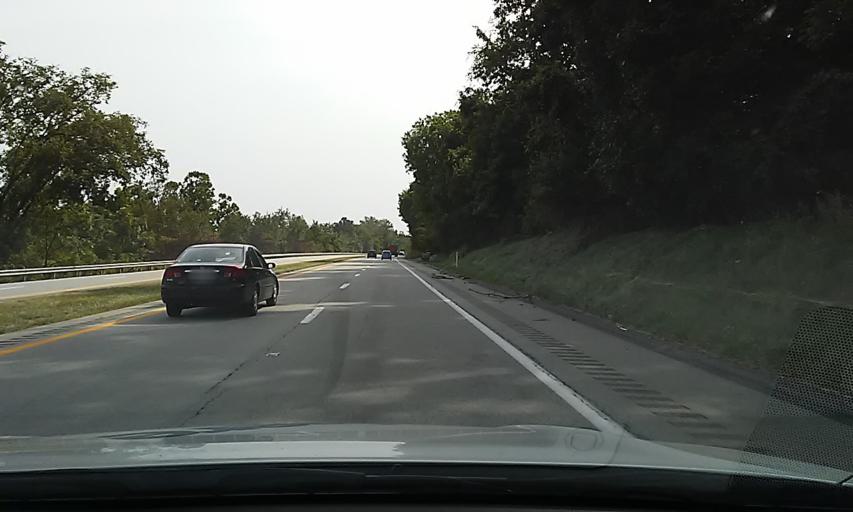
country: US
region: Pennsylvania
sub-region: Westmoreland County
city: Scottdale
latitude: 40.0784
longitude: -79.5623
